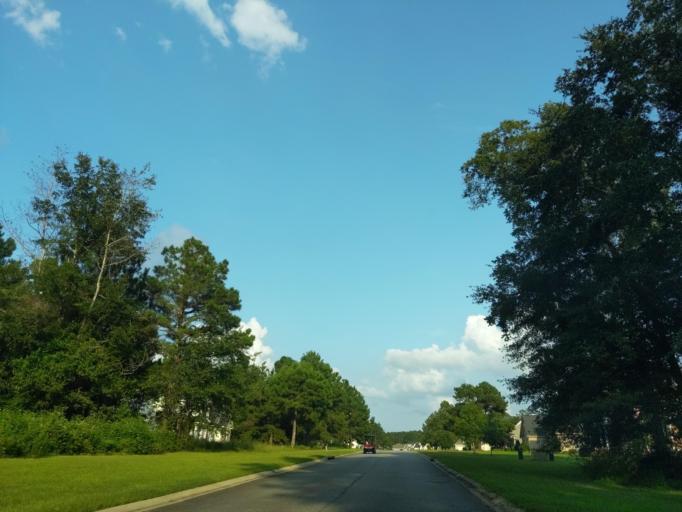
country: US
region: Georgia
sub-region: Thomas County
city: Thomasville
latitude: 30.8984
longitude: -83.9459
